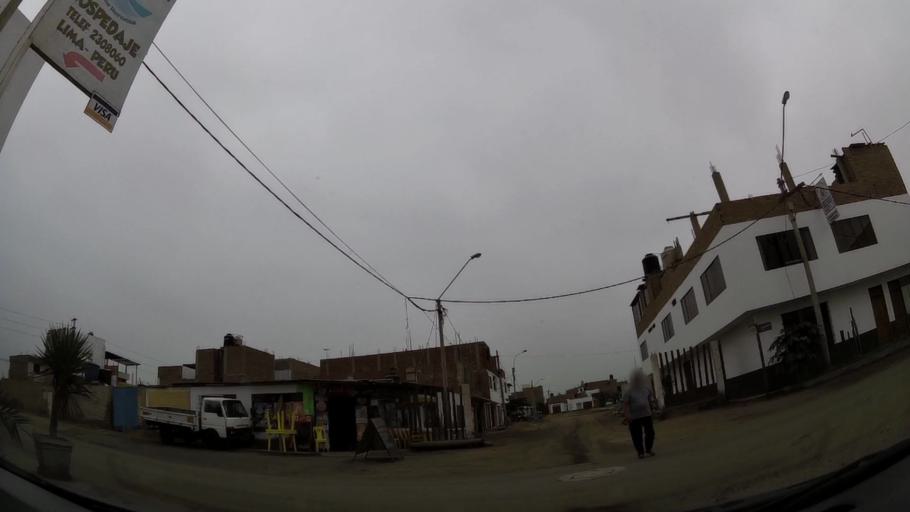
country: PE
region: Lima
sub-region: Lima
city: Punta Hermosa
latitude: -12.3327
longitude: -76.8266
